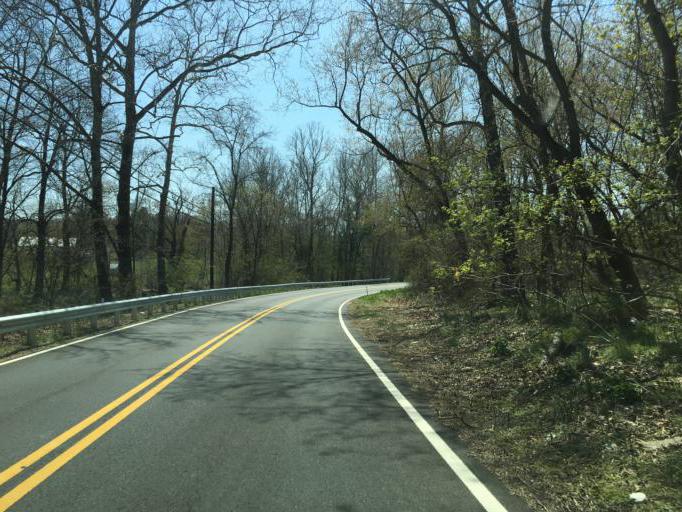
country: US
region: Maryland
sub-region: Frederick County
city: Myersville
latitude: 39.5278
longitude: -77.5355
